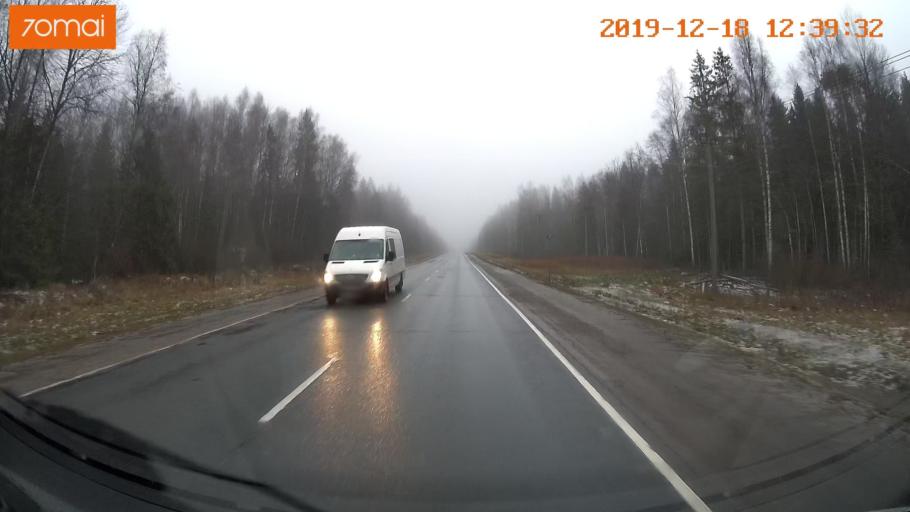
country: RU
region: Moskovskaya
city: Vysokovsk
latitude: 56.1661
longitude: 36.6120
